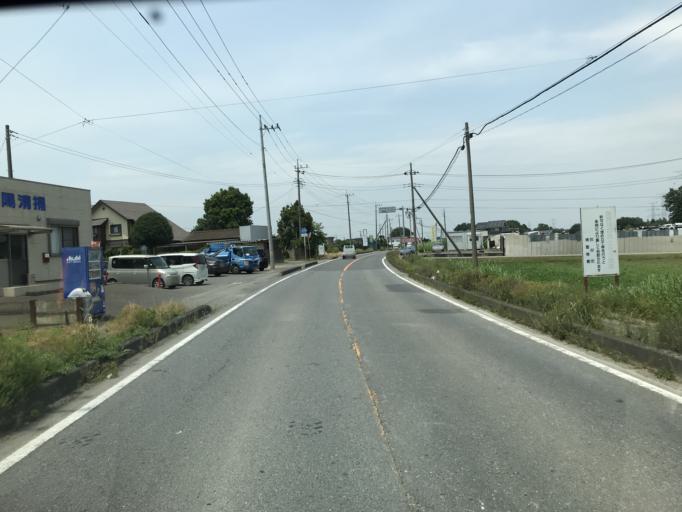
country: JP
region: Ibaraki
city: Iwai
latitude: 36.0034
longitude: 139.8863
